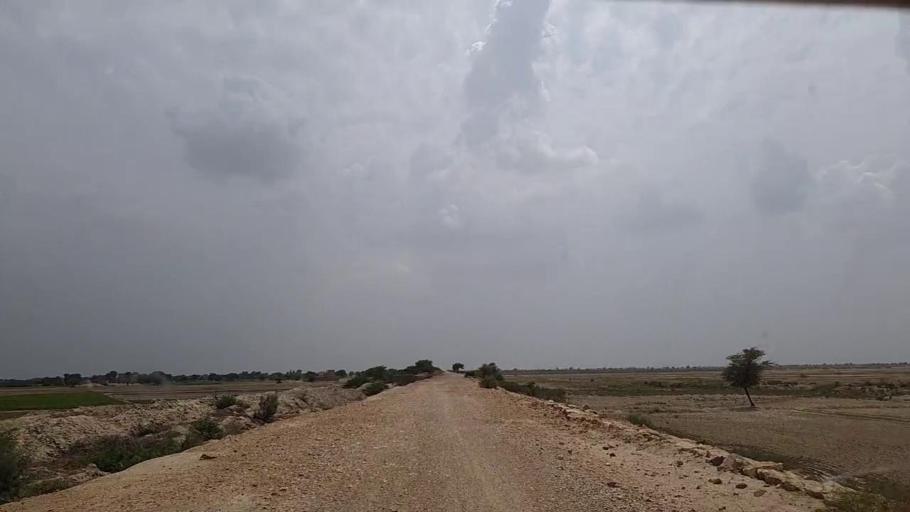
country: PK
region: Sindh
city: Johi
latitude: 26.7399
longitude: 67.5843
